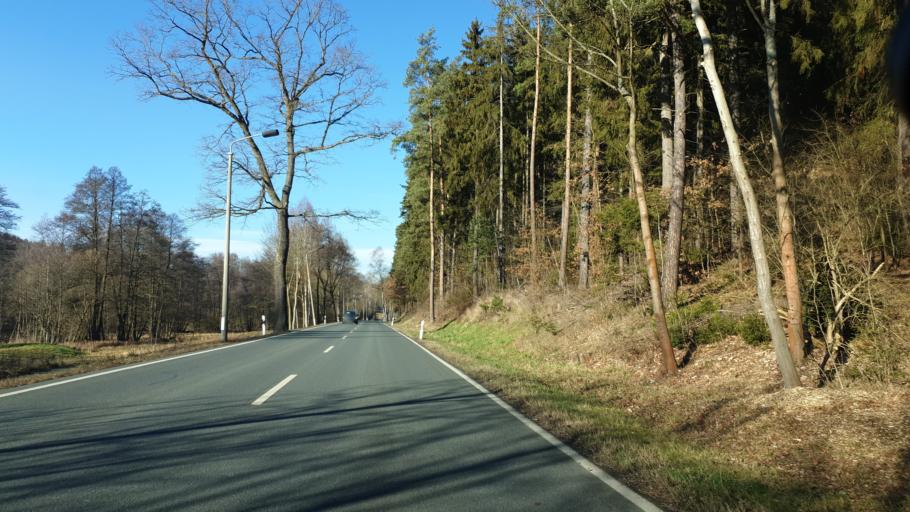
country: DE
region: Saxony
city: Adorf
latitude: 50.2828
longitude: 12.2782
